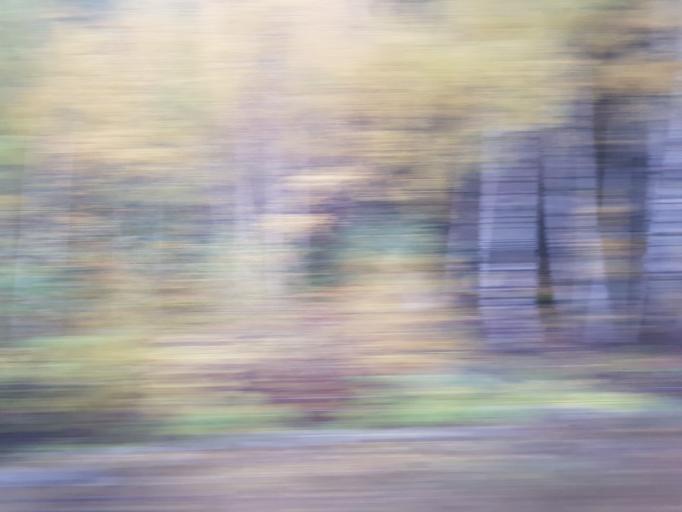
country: NO
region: Oppland
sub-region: Sel
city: Otta
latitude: 61.8396
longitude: 9.4509
